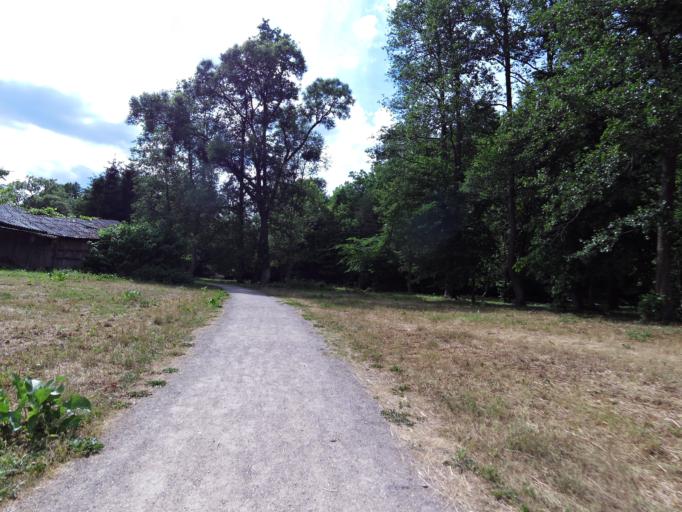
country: LT
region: Vilnius County
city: Rasos
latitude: 54.6899
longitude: 25.3599
